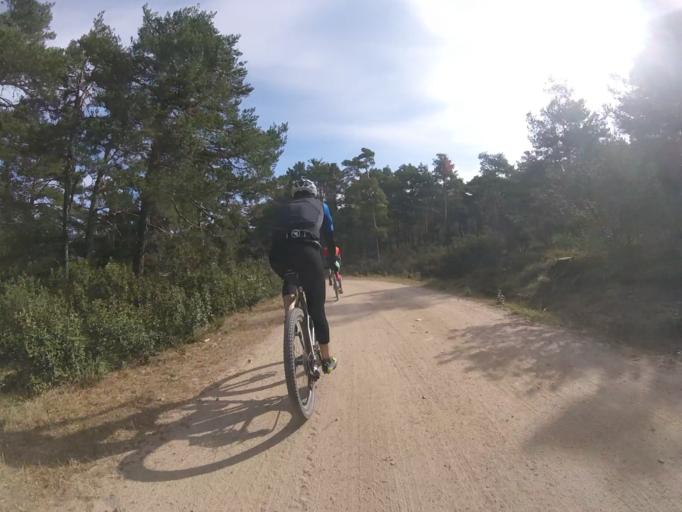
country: ES
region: Castille and Leon
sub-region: Provincia de Avila
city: Peguerinos
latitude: 40.6486
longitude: -4.1777
